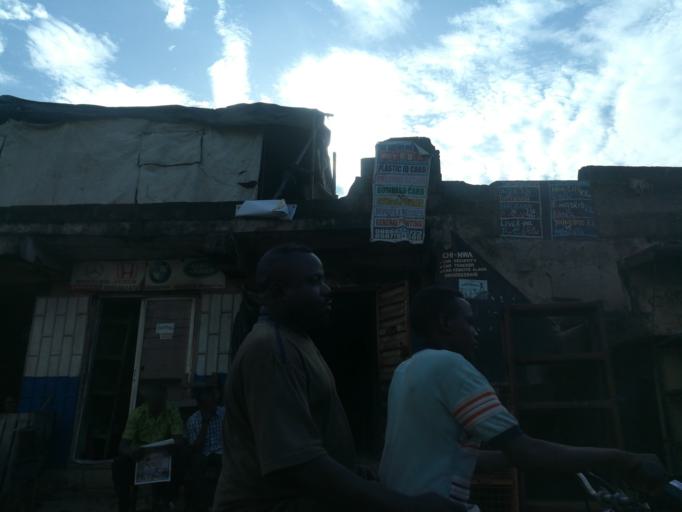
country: NG
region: Lagos
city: Ikeja
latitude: 6.5961
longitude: 3.3445
